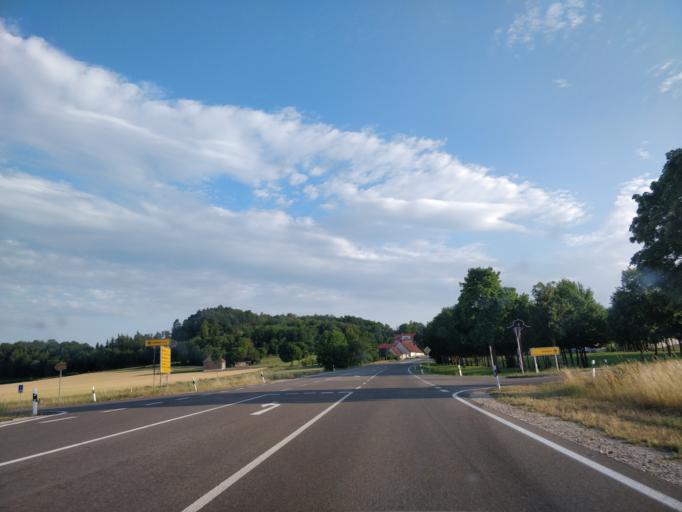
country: DE
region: Bavaria
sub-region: Swabia
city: Ederheim
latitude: 48.8243
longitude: 10.4638
